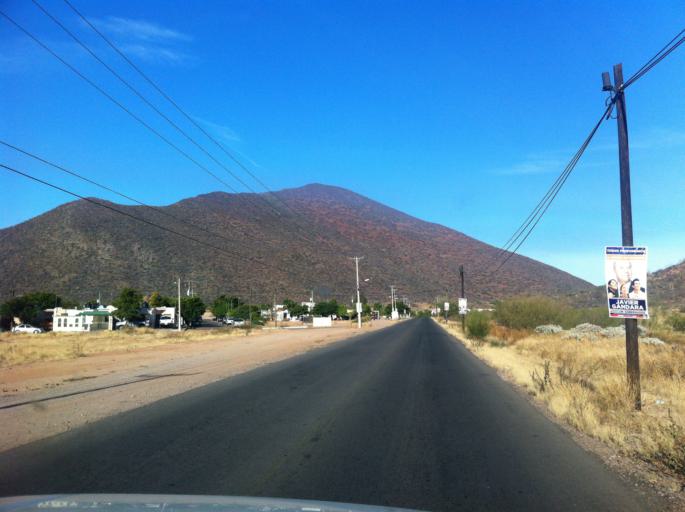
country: MX
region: Sonora
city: Heroica Guaymas
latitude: 27.9293
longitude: -110.9380
